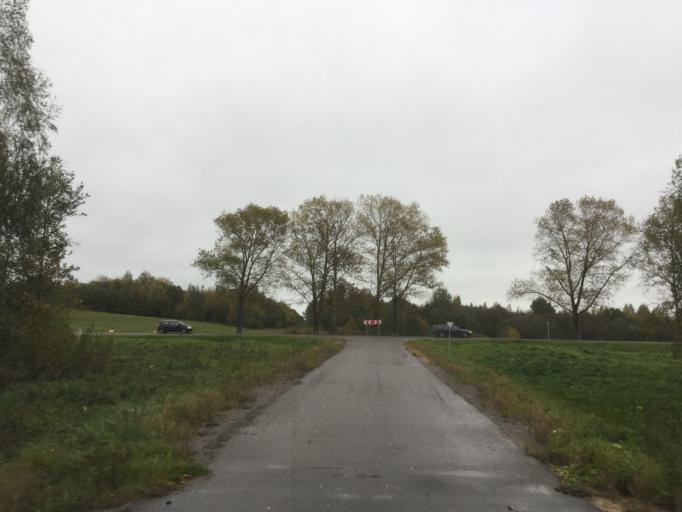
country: BY
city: Novolukoml'
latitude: 54.7332
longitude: 29.1422
